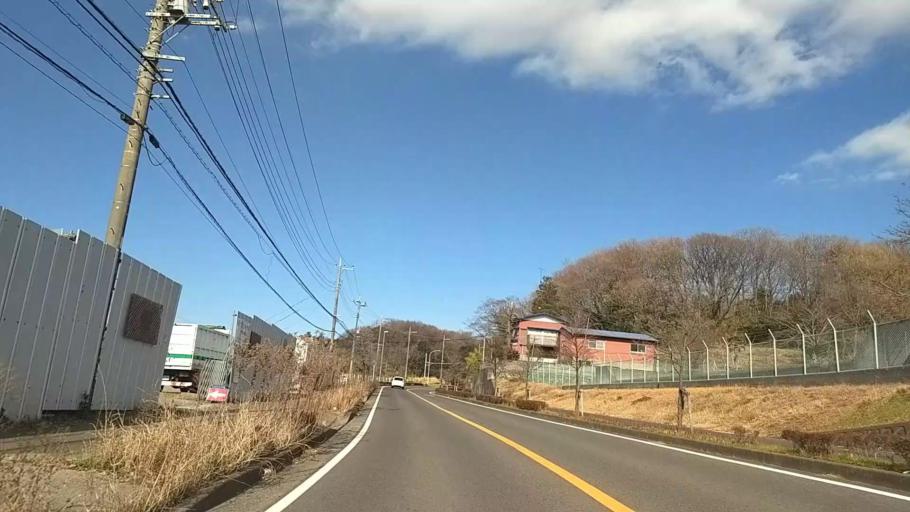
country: JP
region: Kanagawa
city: Isehara
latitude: 35.4248
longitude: 139.3026
